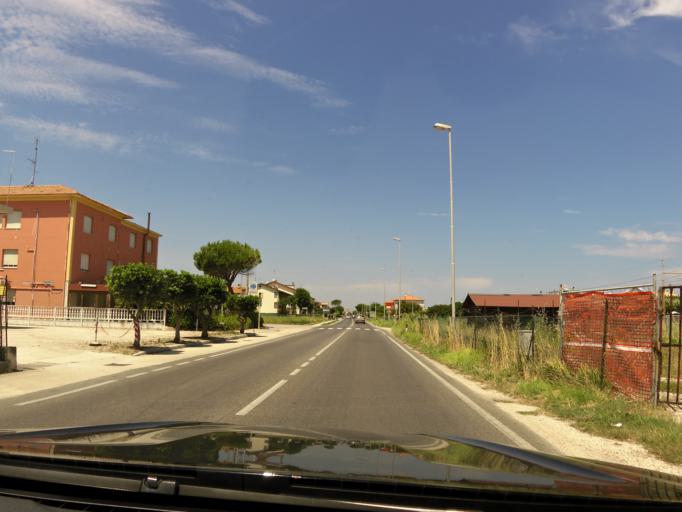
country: IT
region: The Marches
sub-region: Provincia di Pesaro e Urbino
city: Marotta
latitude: 43.7803
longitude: 13.1204
